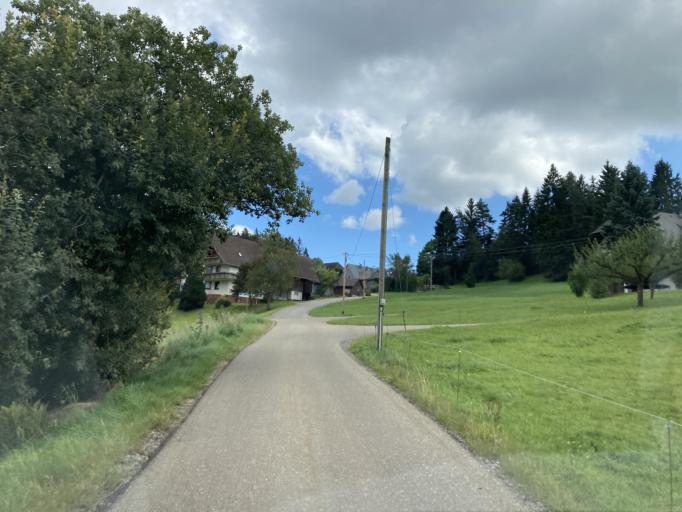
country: DE
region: Baden-Wuerttemberg
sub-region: Freiburg Region
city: Sankt Georgen im Schwarzwald
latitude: 48.1053
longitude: 8.3385
